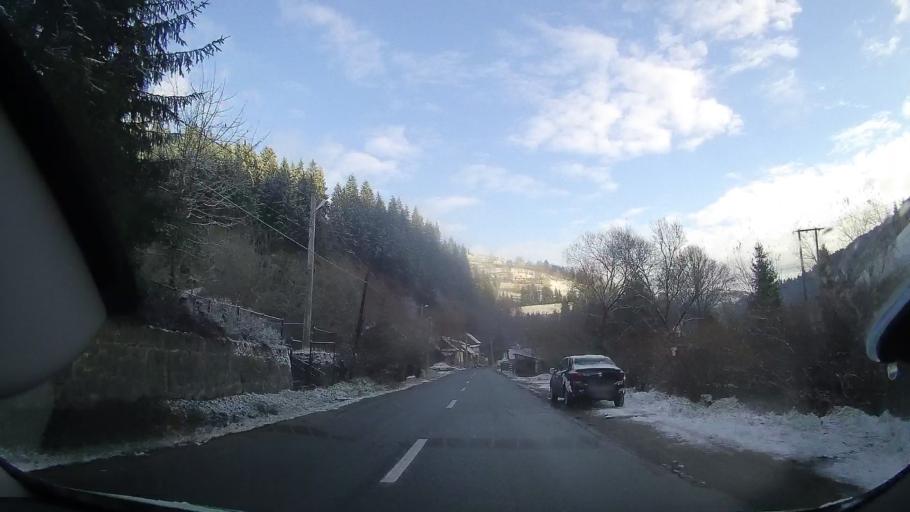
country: RO
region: Alba
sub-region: Comuna Scarisoara
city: Scarisoara
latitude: 46.4563
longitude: 22.8668
